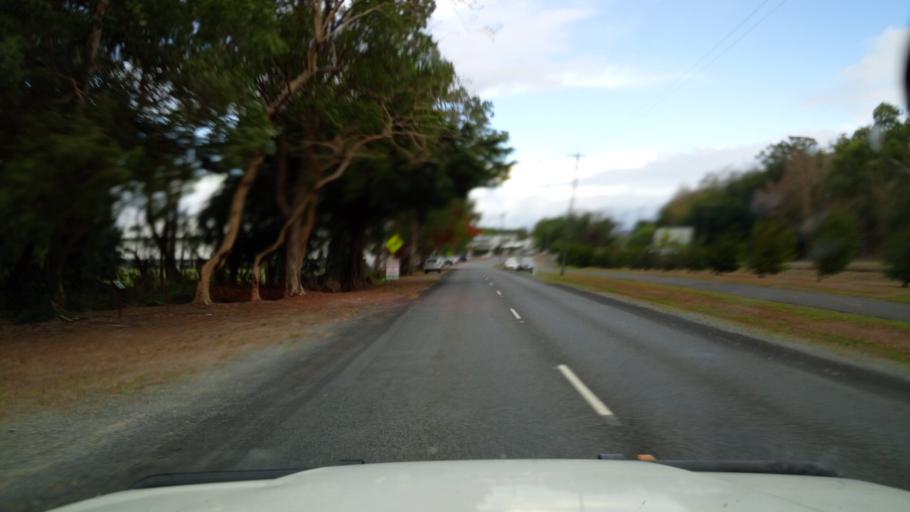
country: AU
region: Queensland
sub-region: Cairns
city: Redlynch
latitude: -16.8746
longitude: 145.7375
